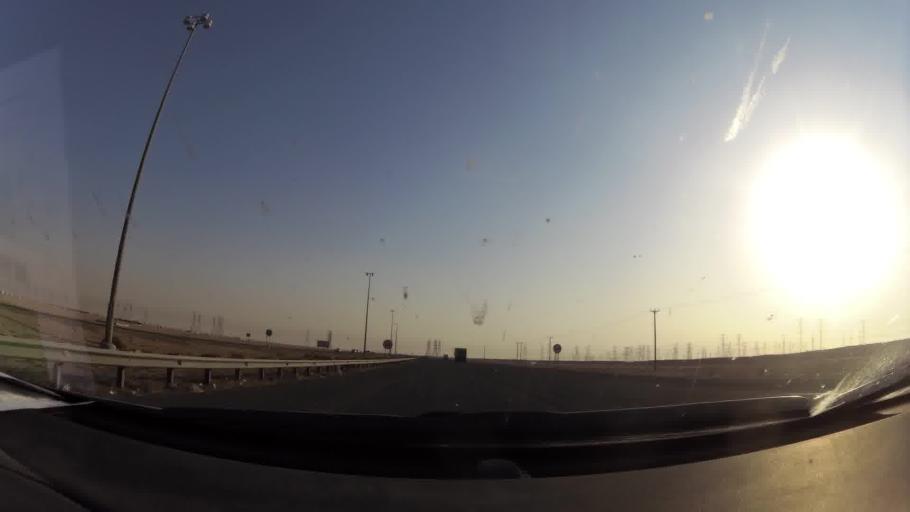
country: KW
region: Muhafazat al Jahra'
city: Al Jahra'
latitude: 29.5710
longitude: 47.6541
